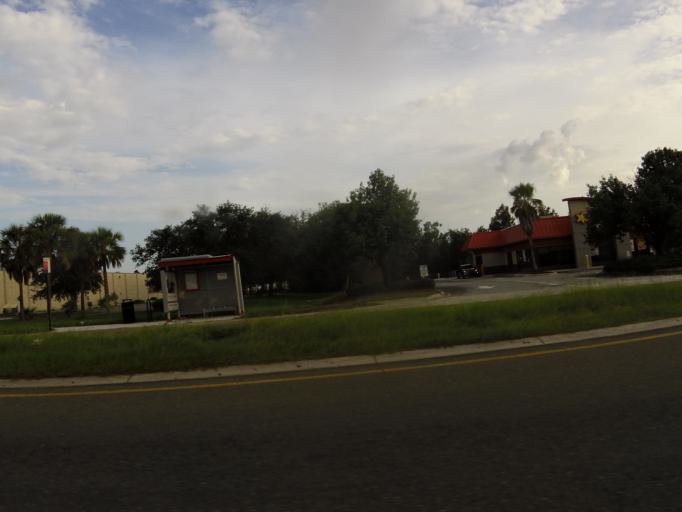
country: US
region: Florida
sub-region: Duval County
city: Jacksonville
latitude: 30.3358
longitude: -81.7584
